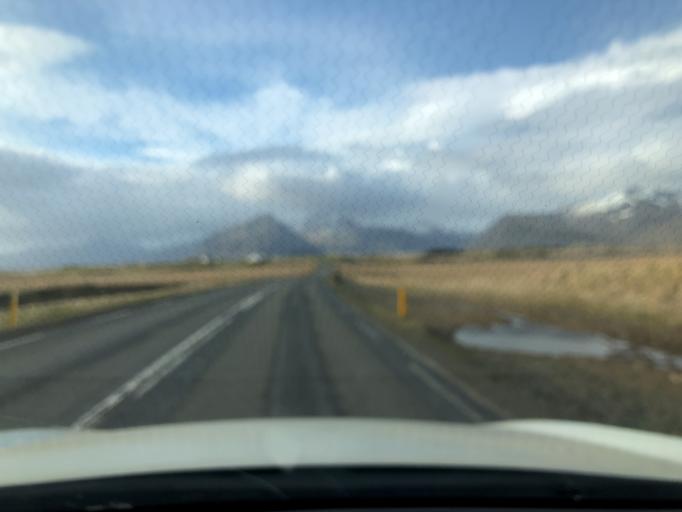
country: IS
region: East
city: Hoefn
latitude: 64.2698
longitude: -15.2024
